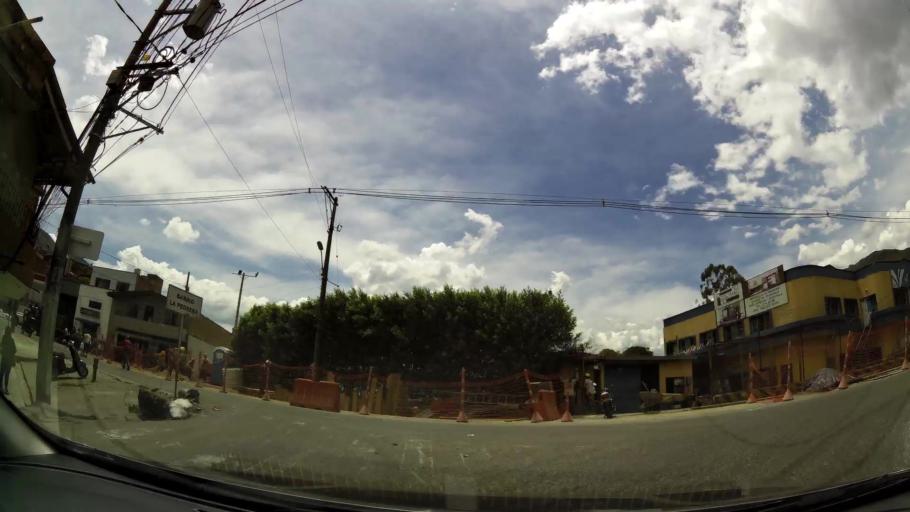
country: CO
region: Antioquia
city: Municipio de Copacabana
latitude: 6.3493
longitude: -75.5074
